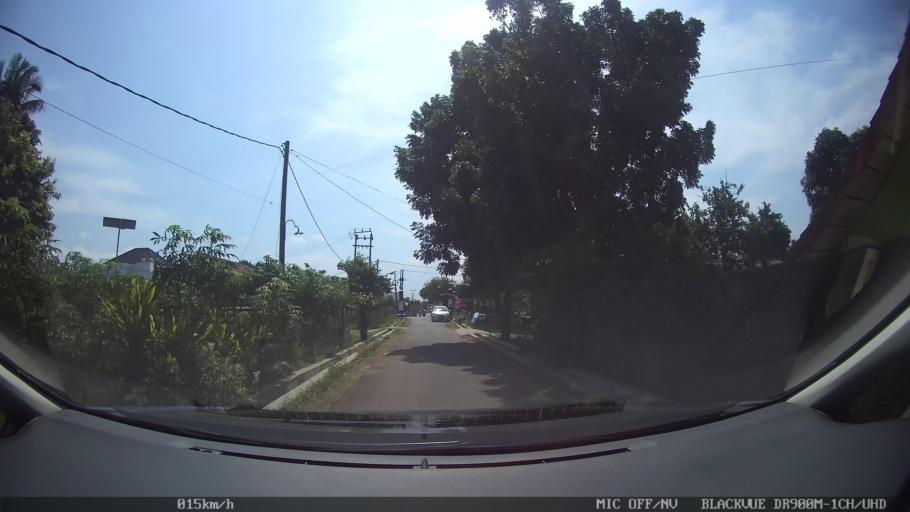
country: ID
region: Lampung
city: Kedaton
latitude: -5.3609
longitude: 105.2538
